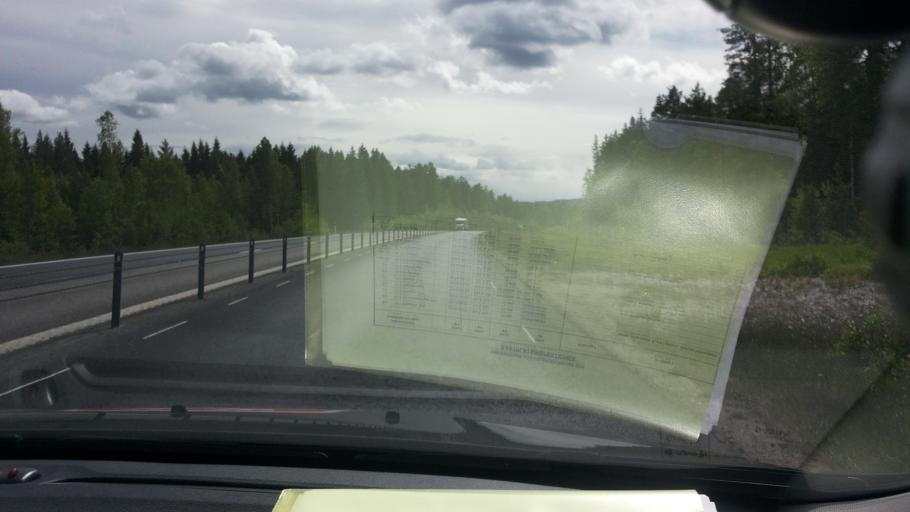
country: SE
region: Vaesternorrland
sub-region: Sundsvalls Kommun
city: Njurundabommen
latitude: 62.1959
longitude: 17.3696
